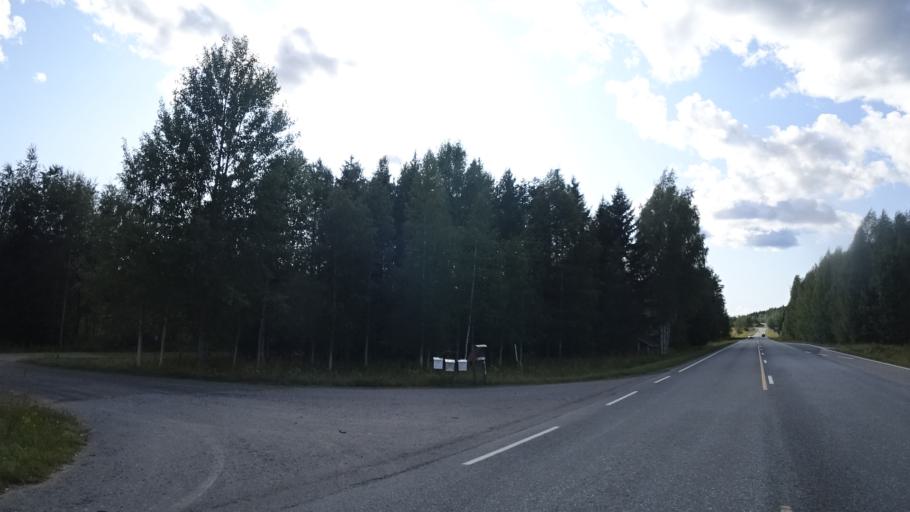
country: FI
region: North Karelia
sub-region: Keski-Karjala
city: Kitee
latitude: 62.0901
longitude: 29.9730
